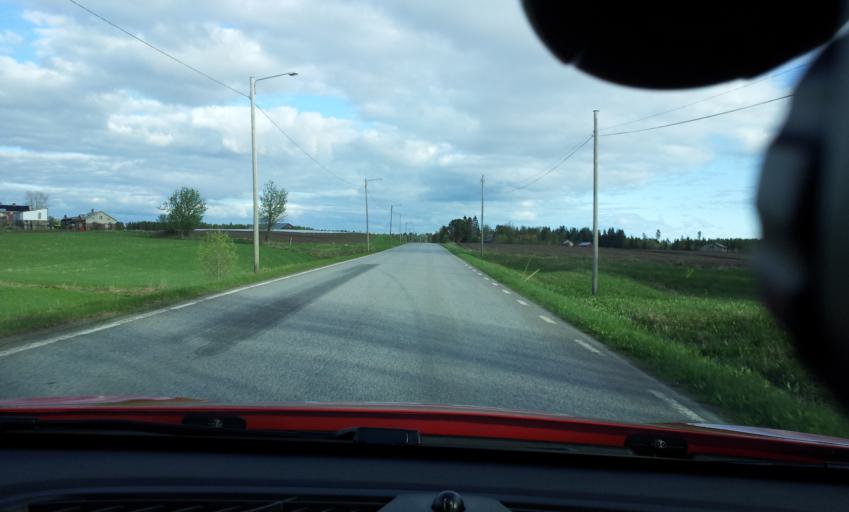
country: SE
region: Jaemtland
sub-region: Krokoms Kommun
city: Krokom
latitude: 63.2653
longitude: 14.3942
